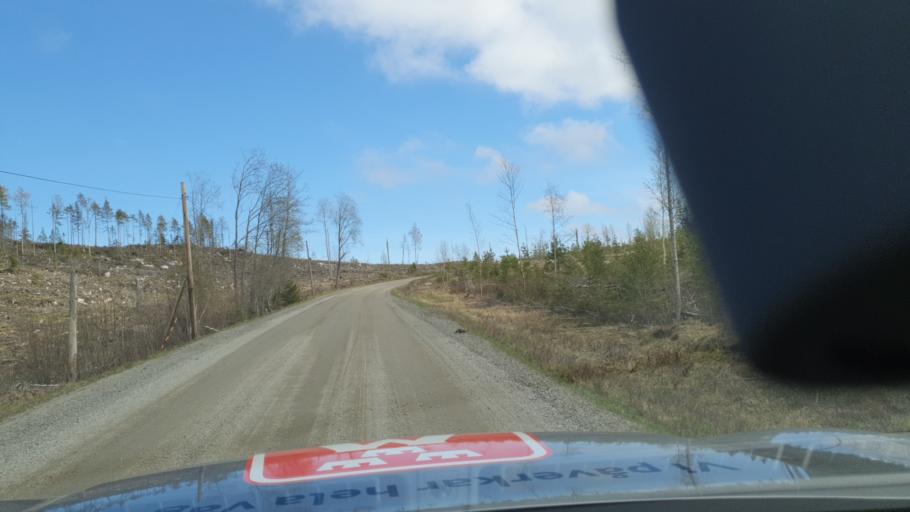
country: SE
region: Vaesterbotten
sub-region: Bjurholms Kommun
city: Bjurholm
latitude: 63.7057
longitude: 18.9070
